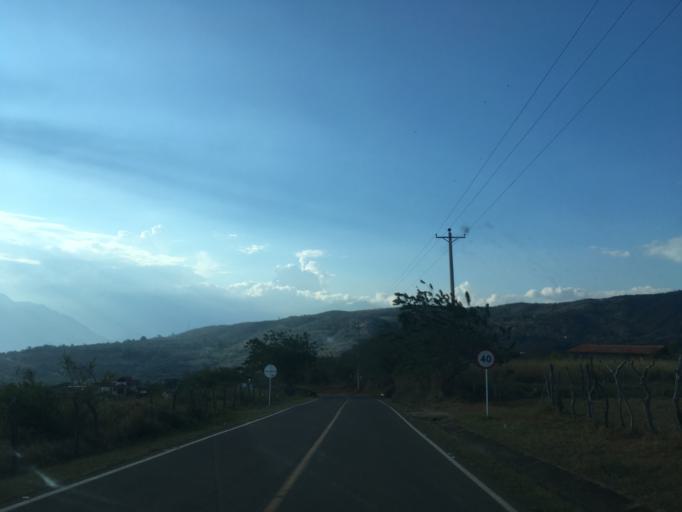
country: CO
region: Santander
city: Villanueva
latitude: 6.6405
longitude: -73.1887
